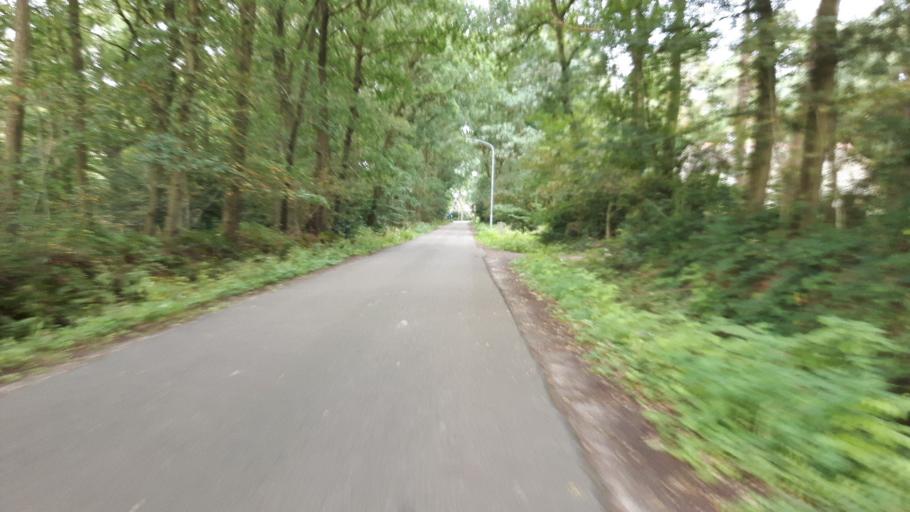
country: NL
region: Groningen
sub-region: Gemeente Leek
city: Leek
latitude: 53.1124
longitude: 6.4295
